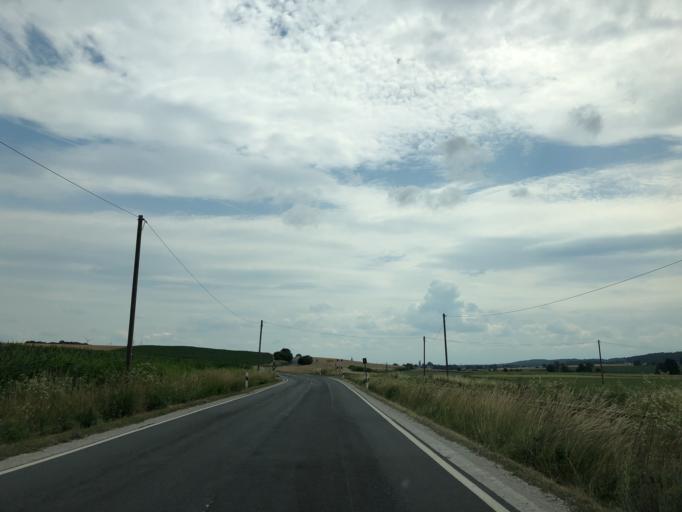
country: DE
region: Bavaria
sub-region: Regierungsbezirk Mittelfranken
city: Wachenroth
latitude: 49.7484
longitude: 10.6873
